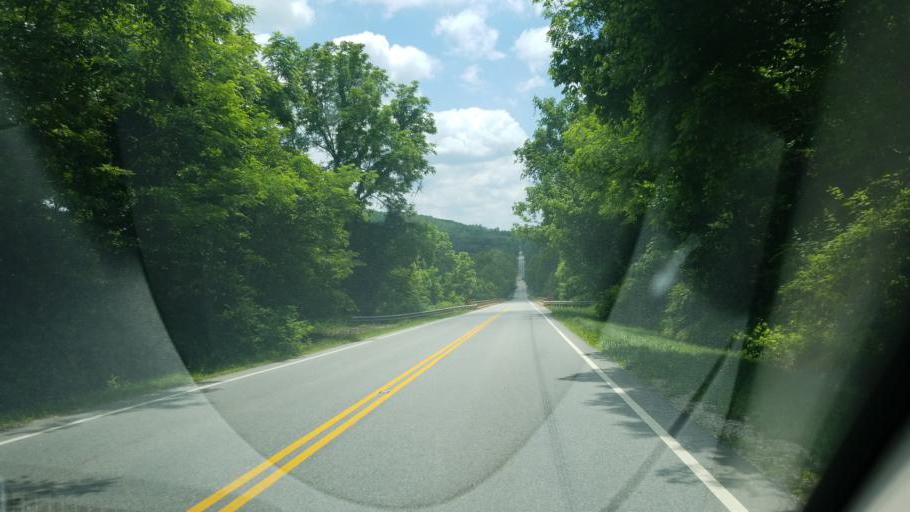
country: US
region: Virginia
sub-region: Appomattox County
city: Appomattox
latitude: 37.5419
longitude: -78.8290
